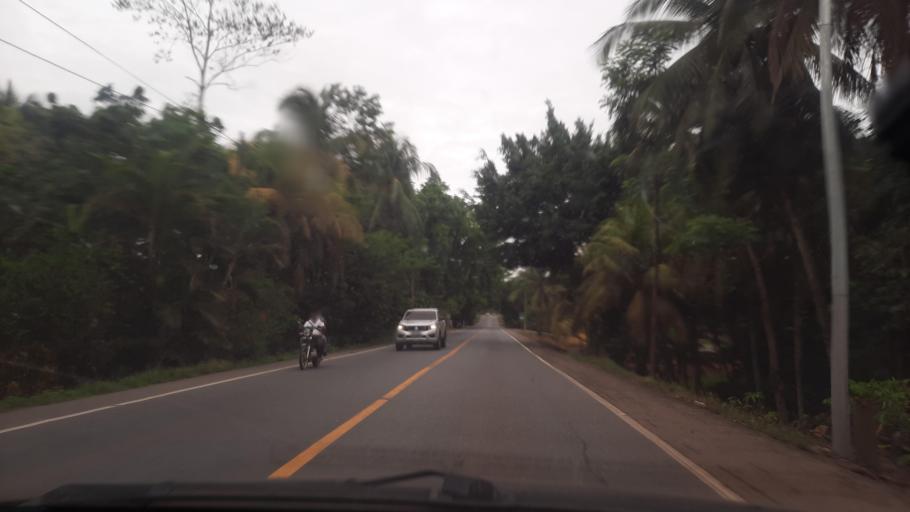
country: GT
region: Izabal
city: Morales
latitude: 15.4279
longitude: -88.9771
